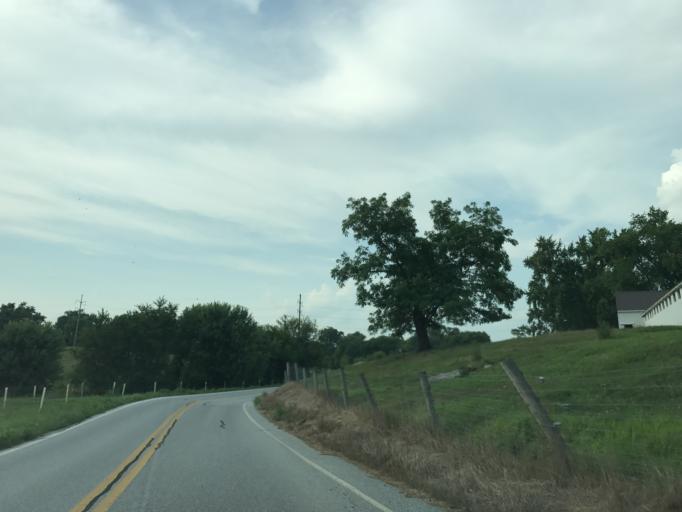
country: US
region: Pennsylvania
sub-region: Lancaster County
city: Mount Joy
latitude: 40.0935
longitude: -76.5355
